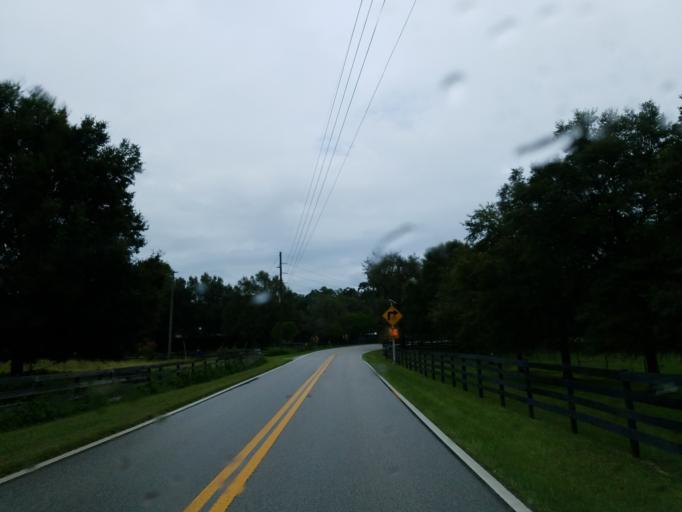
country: US
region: Florida
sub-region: Hernando County
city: Hill 'n Dale
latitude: 28.5859
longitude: -82.3230
